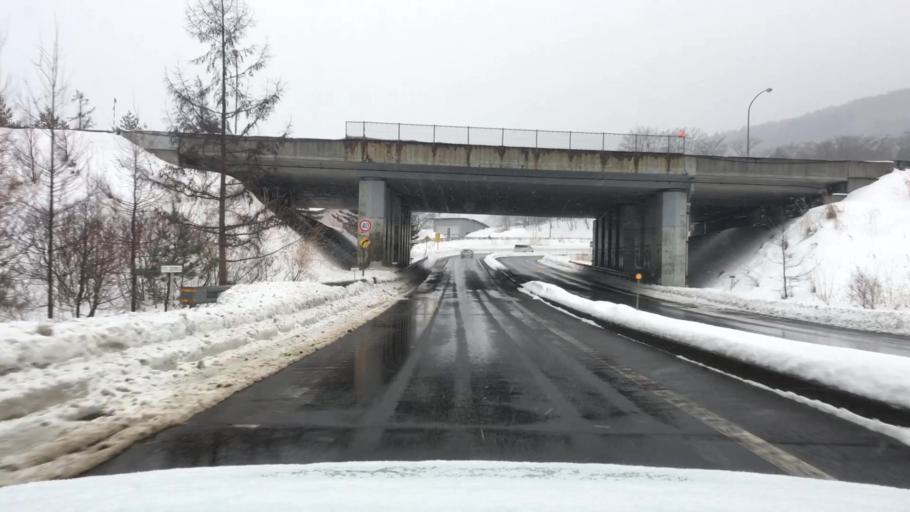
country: JP
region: Iwate
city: Ichinohe
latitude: 40.1099
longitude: 141.0486
